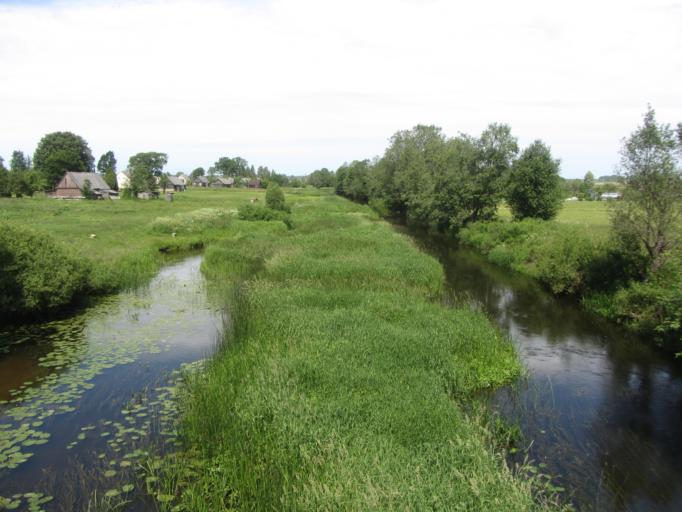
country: LV
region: Nereta
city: Nereta
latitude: 56.1513
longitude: 25.1413
